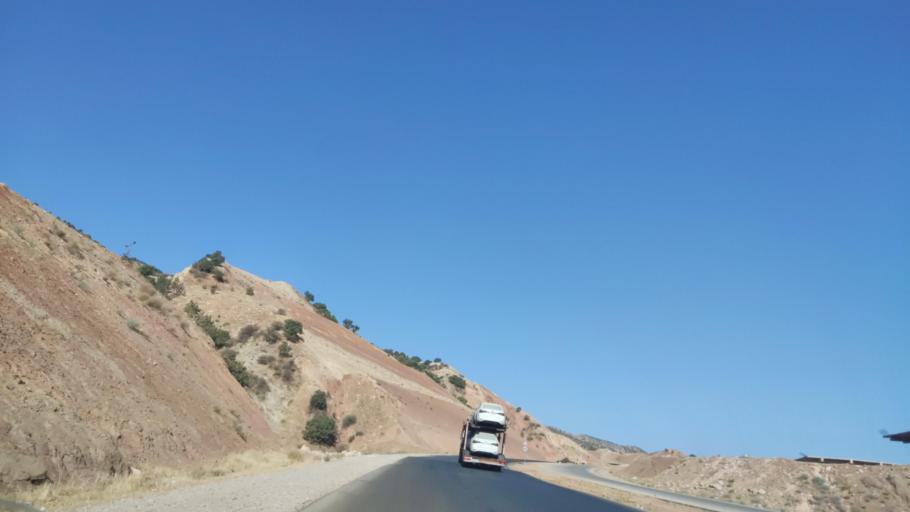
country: IQ
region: Arbil
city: Shaqlawah
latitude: 36.4331
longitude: 44.3047
